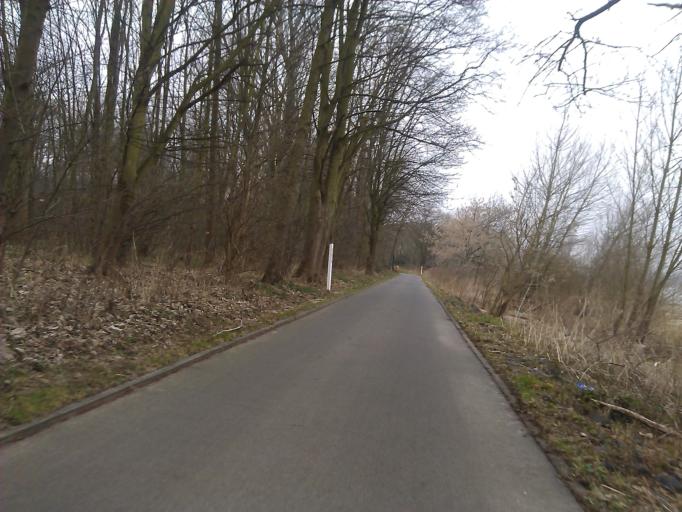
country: DE
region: North Rhine-Westphalia
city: Niederkassel
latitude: 50.8218
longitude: 7.0115
